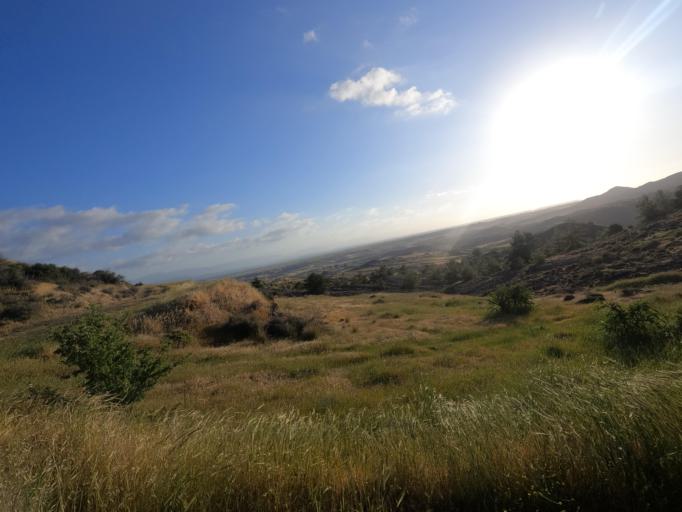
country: CY
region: Lefkosia
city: Astromeritis
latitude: 35.0686
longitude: 33.0361
